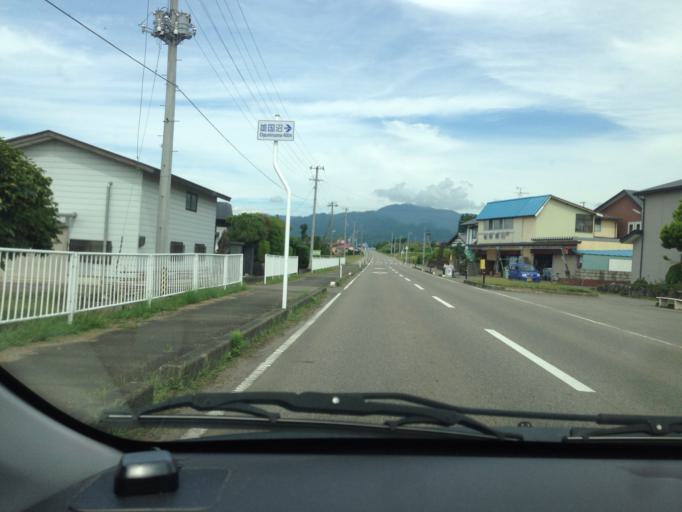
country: JP
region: Fukushima
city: Kitakata
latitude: 37.6219
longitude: 139.9185
